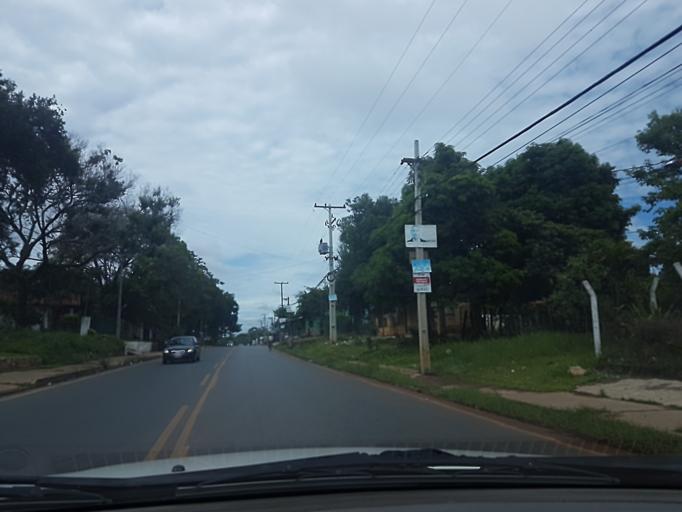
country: PY
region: Central
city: San Lorenzo
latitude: -25.2603
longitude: -57.4775
